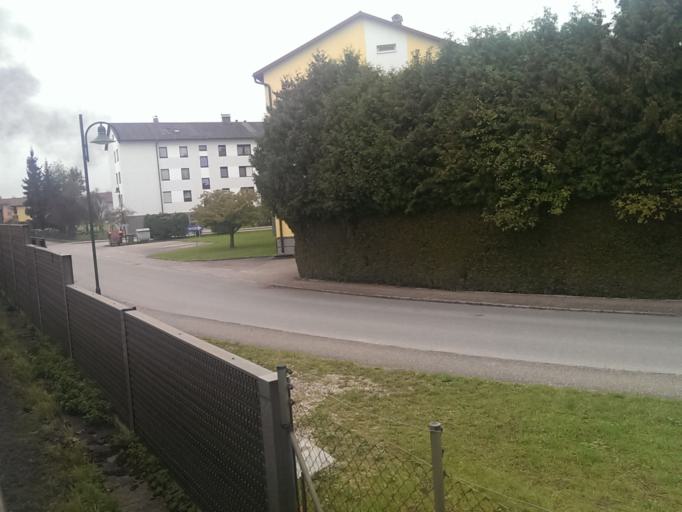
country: AT
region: Upper Austria
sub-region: Politischer Bezirk Vocklabruck
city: Oberndorf bei Schwanenstadt
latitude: 48.0517
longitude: 13.7642
